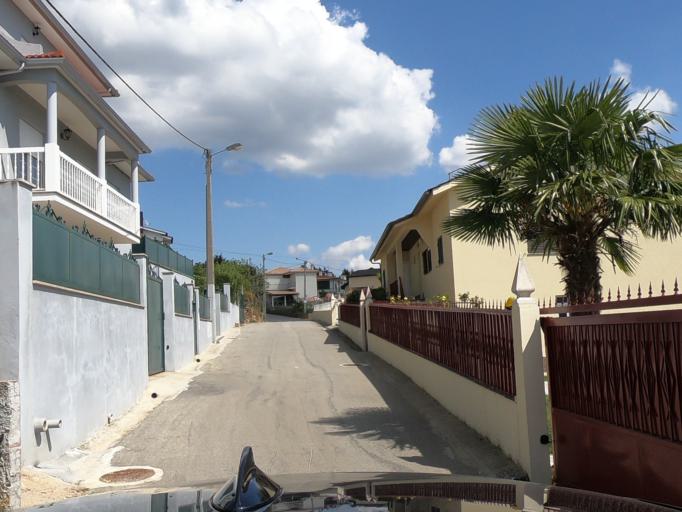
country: PT
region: Vila Real
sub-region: Sabrosa
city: Vilela
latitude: 41.2241
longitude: -7.6901
